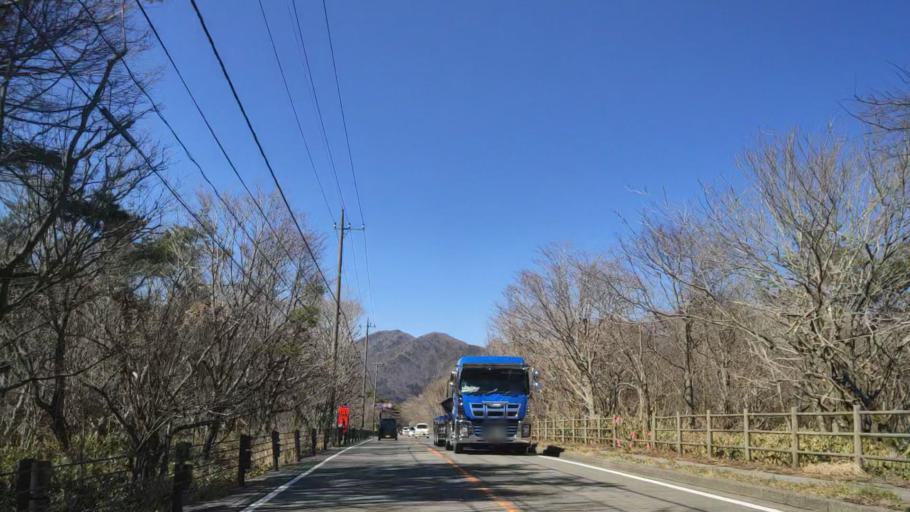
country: JP
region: Yamanashi
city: Fujikawaguchiko
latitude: 35.4483
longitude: 138.6084
